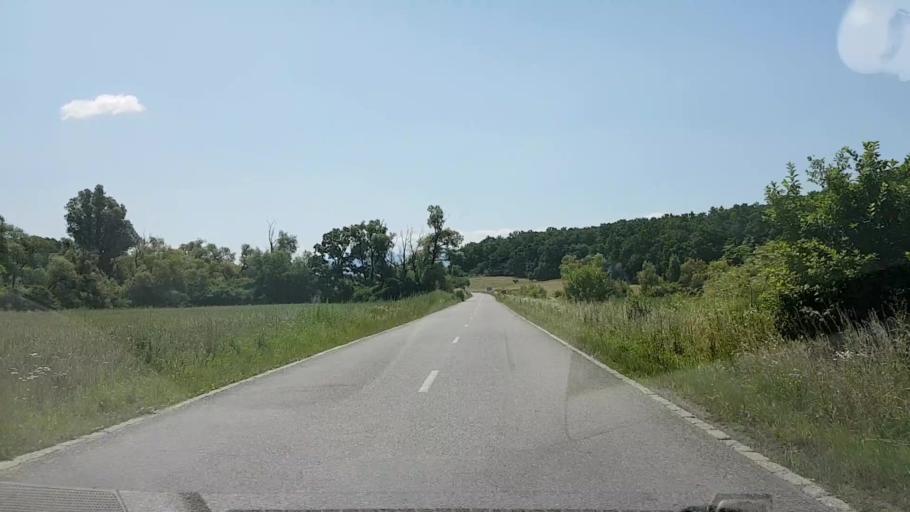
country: RO
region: Brasov
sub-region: Comuna Cincu
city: Cincu
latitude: 45.8736
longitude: 24.8198
